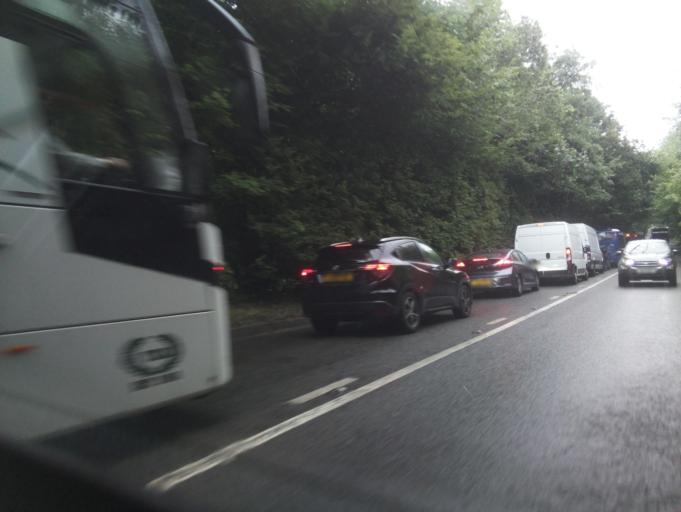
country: GB
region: England
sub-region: Surrey
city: Redhill
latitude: 51.2244
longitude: -0.1731
